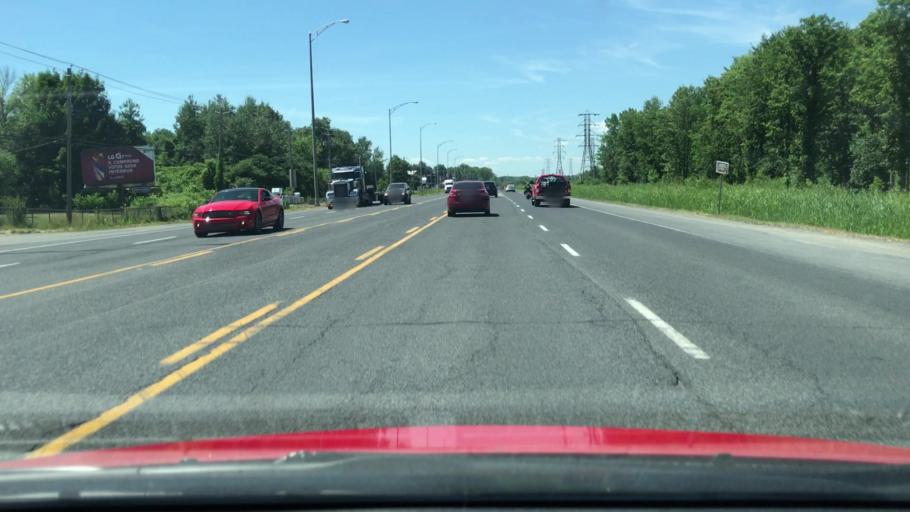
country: CA
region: Quebec
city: Montreal-Ouest
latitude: 45.3977
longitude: -73.6219
